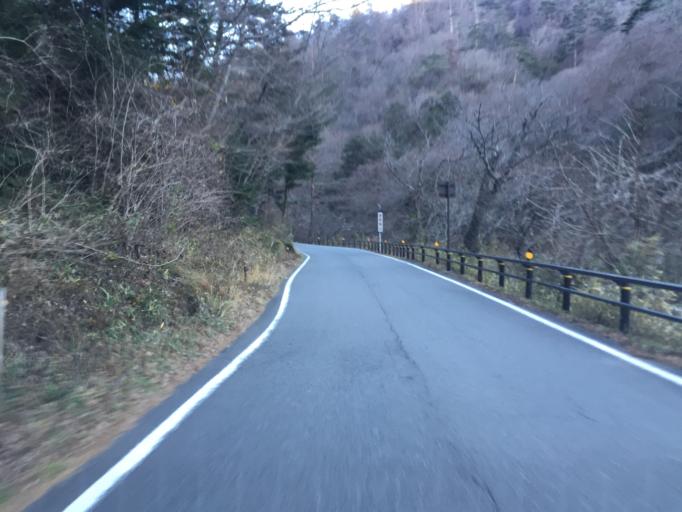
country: JP
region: Fukushima
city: Iwaki
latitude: 37.1907
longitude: 140.8086
